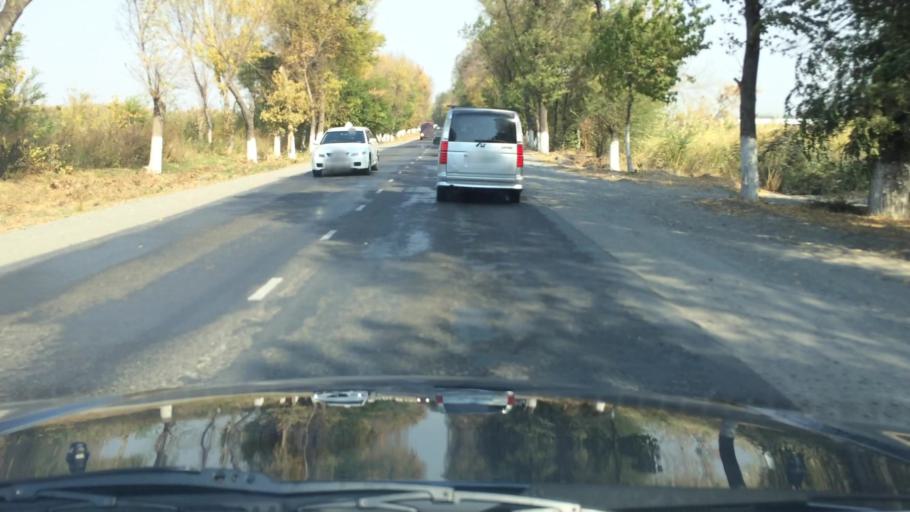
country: KG
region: Chuy
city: Lebedinovka
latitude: 42.9229
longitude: 74.6900
